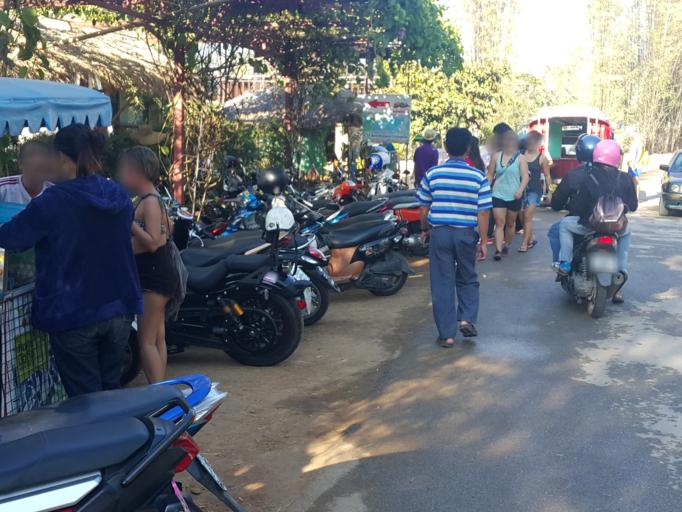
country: TH
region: Chiang Mai
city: Hang Dong
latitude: 18.6969
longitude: 98.8932
